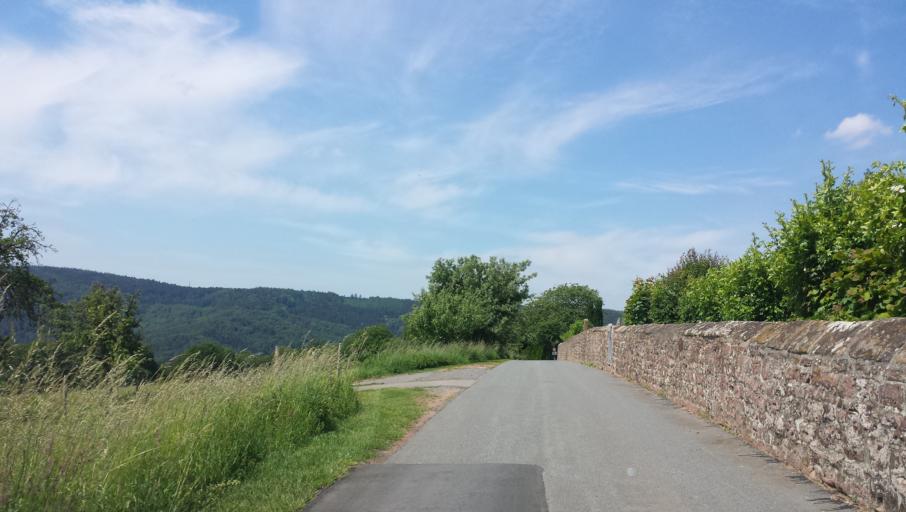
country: DE
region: Hesse
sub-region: Regierungsbezirk Darmstadt
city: Rothenberg
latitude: 49.4990
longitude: 8.9145
